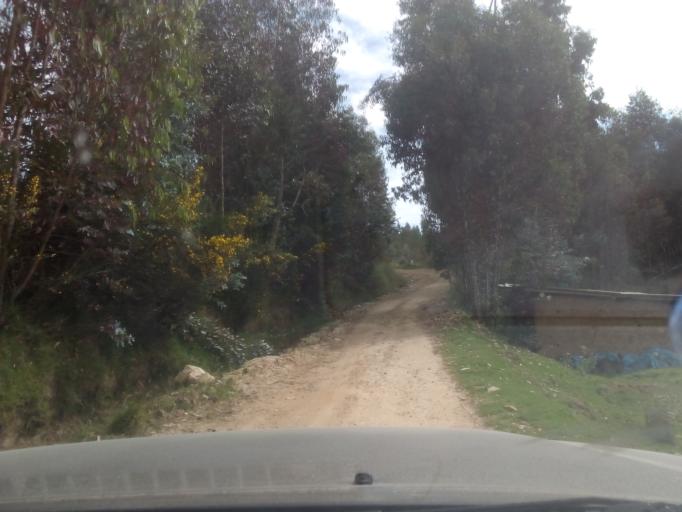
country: PE
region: La Libertad
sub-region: Sanchez Carrion
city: Curgos
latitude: -7.8668
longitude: -77.9705
